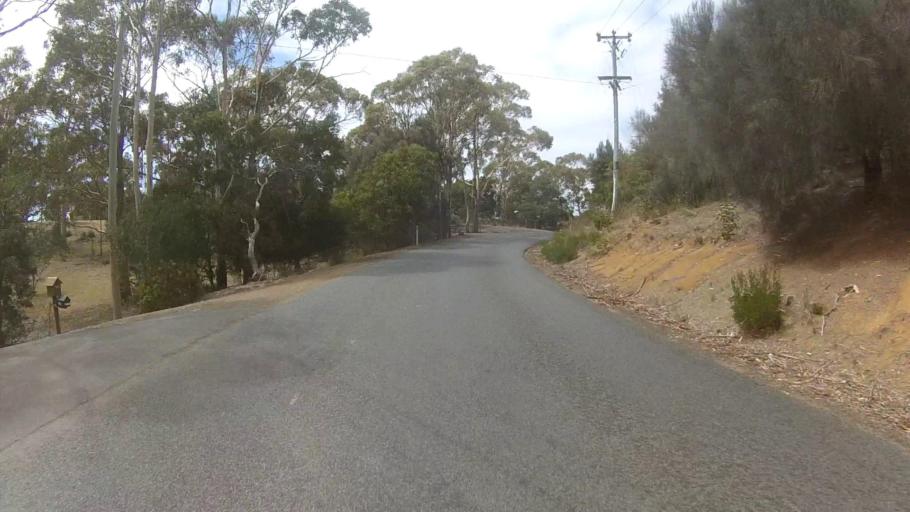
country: AU
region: Tasmania
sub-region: Kingborough
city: Blackmans Bay
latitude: -43.0336
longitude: 147.3314
